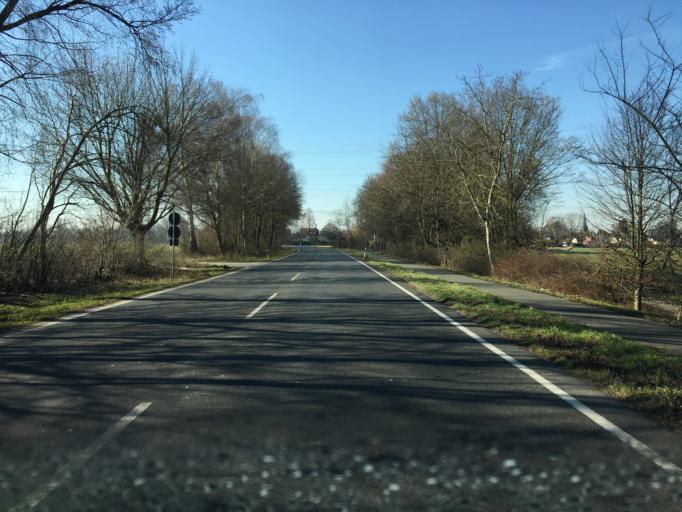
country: DE
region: North Rhine-Westphalia
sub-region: Regierungsbezirk Koln
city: Pulheim
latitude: 50.9845
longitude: 6.7959
